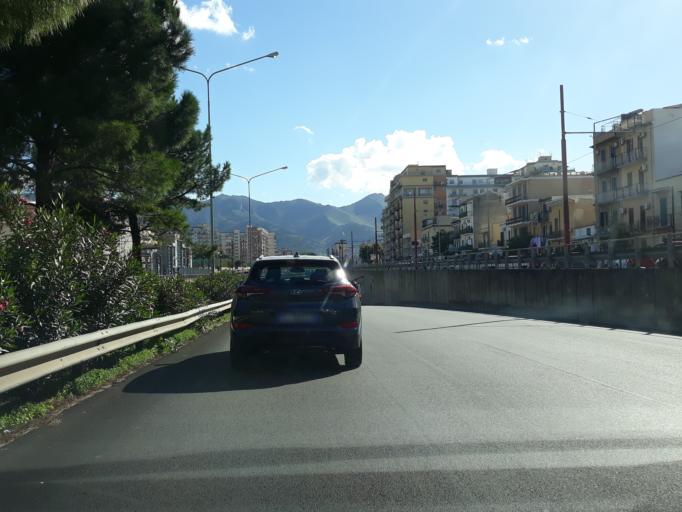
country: IT
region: Sicily
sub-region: Palermo
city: Palermo
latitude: 38.1124
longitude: 13.3295
